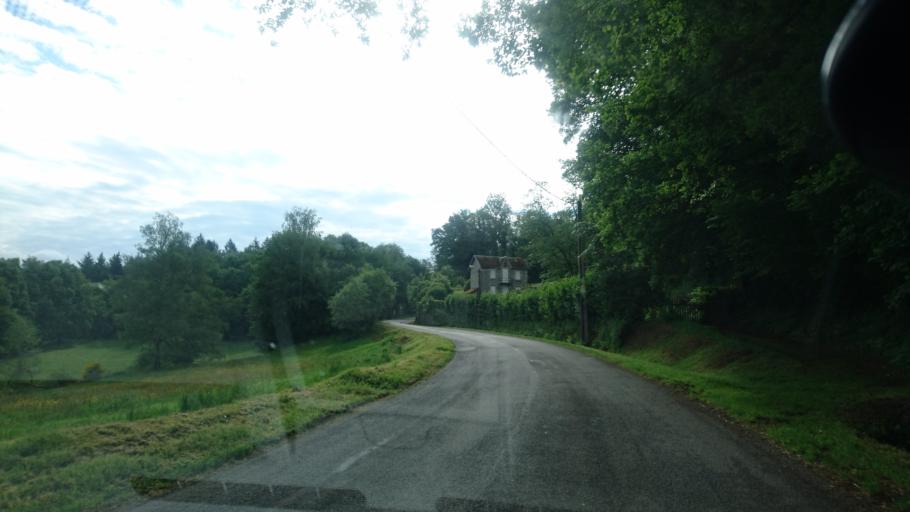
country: FR
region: Limousin
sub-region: Departement de la Haute-Vienne
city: Peyrat-le-Chateau
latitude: 45.8111
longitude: 1.7830
